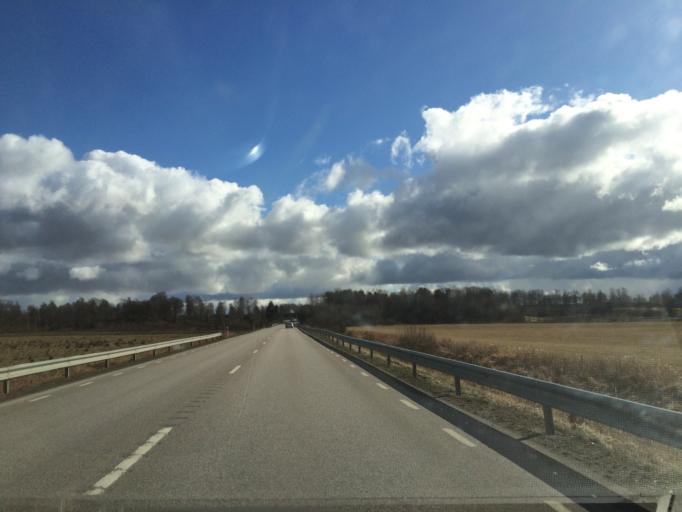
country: SE
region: Vaestra Goetaland
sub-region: Skara Kommun
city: Skara
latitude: 58.2905
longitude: 13.4775
